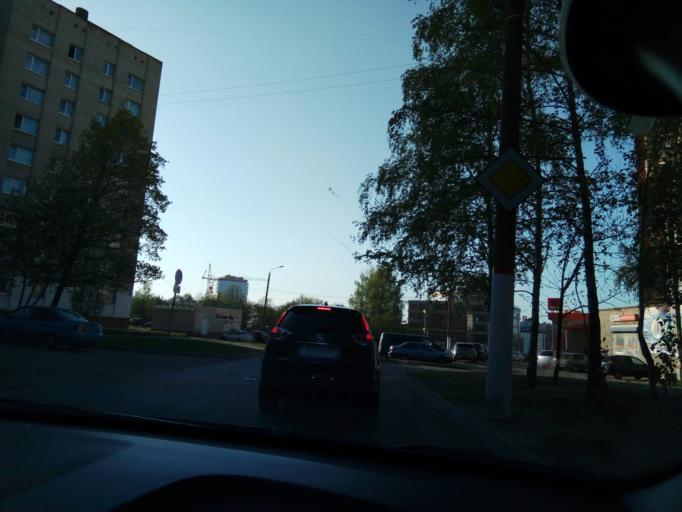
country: RU
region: Chuvashia
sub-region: Cheboksarskiy Rayon
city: Cheboksary
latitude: 56.1475
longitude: 47.1908
